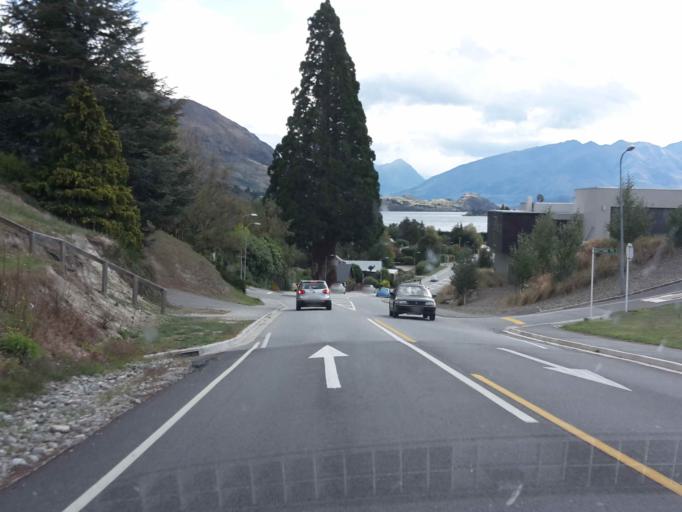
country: NZ
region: Otago
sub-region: Queenstown-Lakes District
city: Wanaka
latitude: -44.7050
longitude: 169.1348
